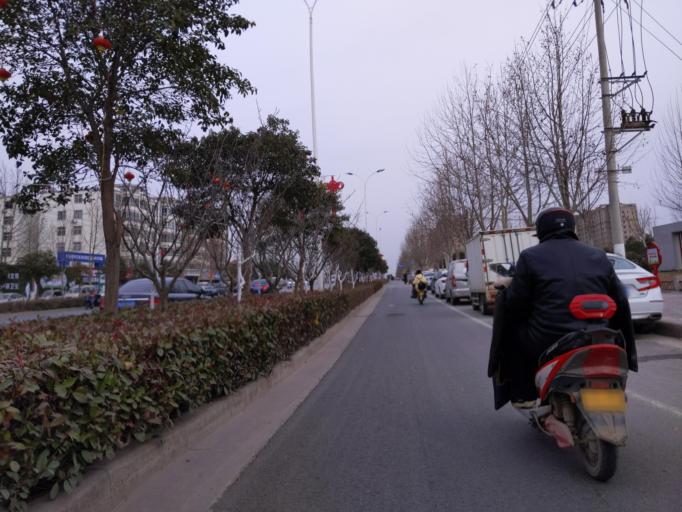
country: CN
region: Henan Sheng
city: Zhongyuanlu
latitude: 35.7568
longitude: 115.0797
